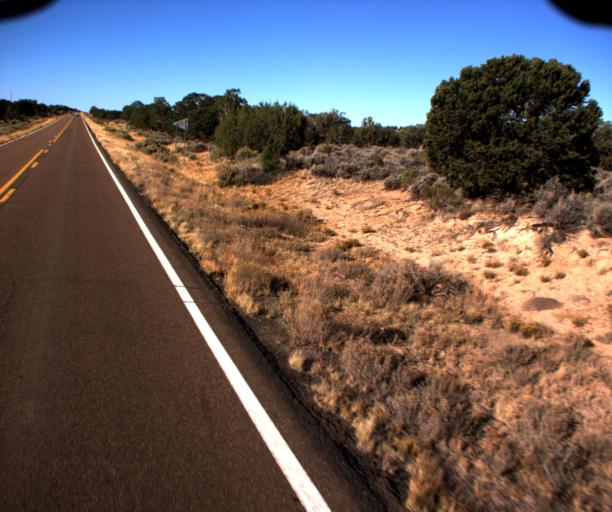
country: US
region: Arizona
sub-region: Apache County
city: Ganado
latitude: 35.7513
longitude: -109.9070
